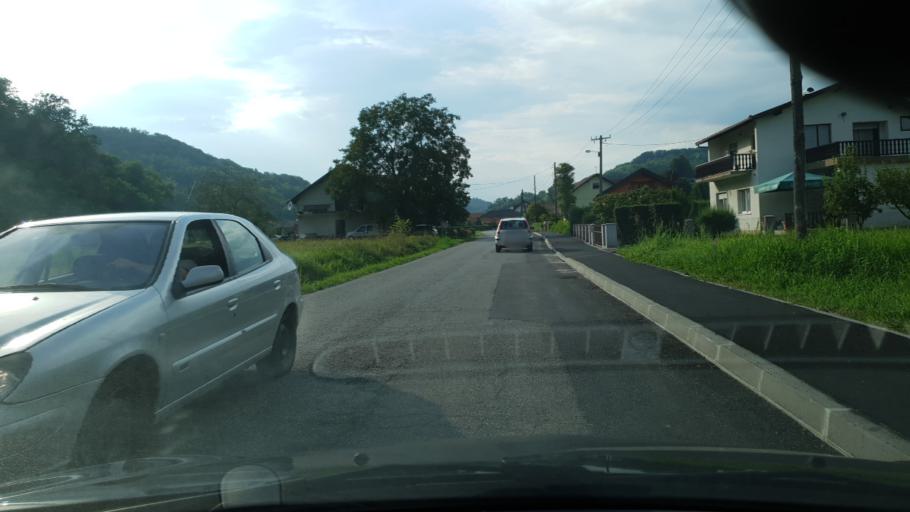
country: HR
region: Krapinsko-Zagorska
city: Zabok
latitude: 46.0809
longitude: 15.8960
